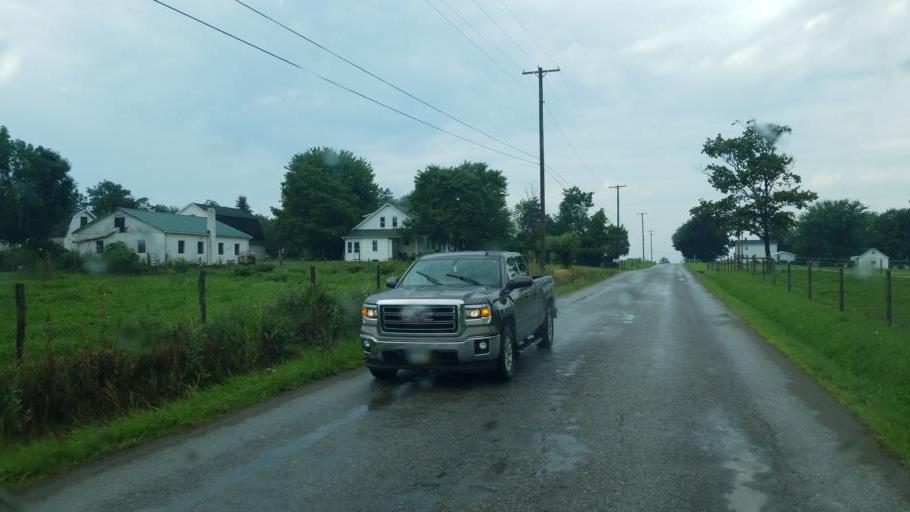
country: US
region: Ohio
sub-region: Geauga County
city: Middlefield
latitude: 41.4792
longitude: -81.0114
